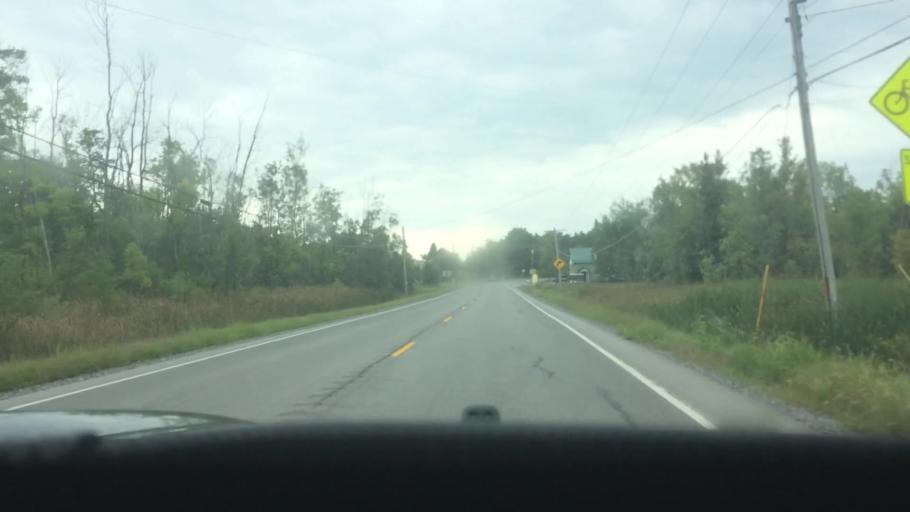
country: US
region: New York
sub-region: St. Lawrence County
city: Ogdensburg
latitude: 44.6245
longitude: -75.4146
